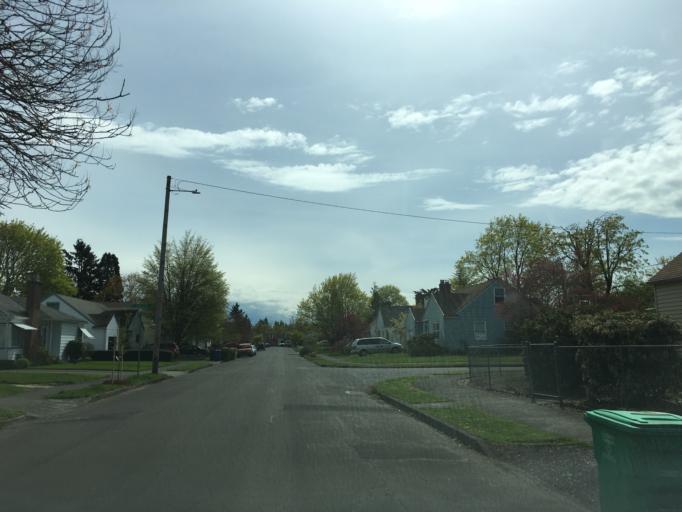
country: US
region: Oregon
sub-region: Multnomah County
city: Lents
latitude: 45.5471
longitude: -122.5730
